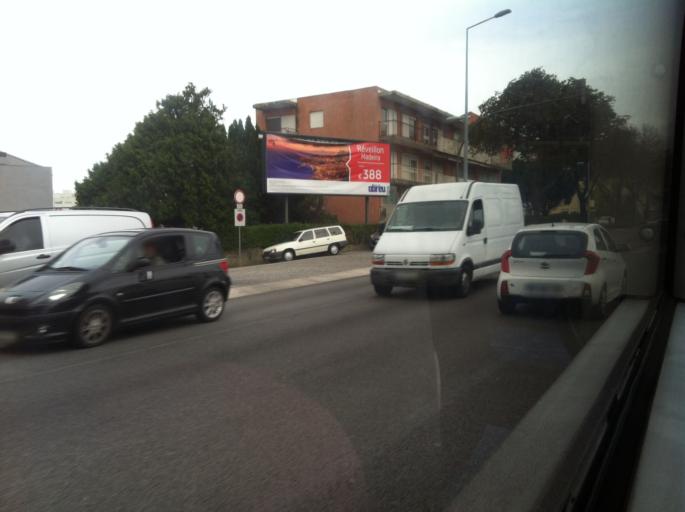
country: PT
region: Porto
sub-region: Matosinhos
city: Senhora da Hora
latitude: 41.1644
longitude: -8.6366
